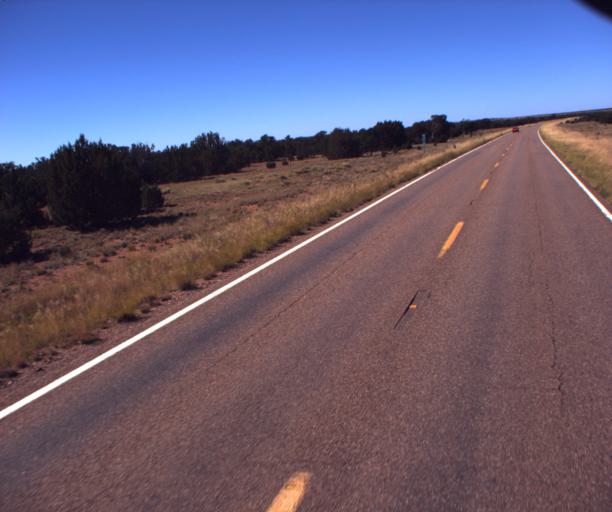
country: US
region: Arizona
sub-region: Navajo County
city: Heber-Overgaard
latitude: 34.4616
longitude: -110.3879
